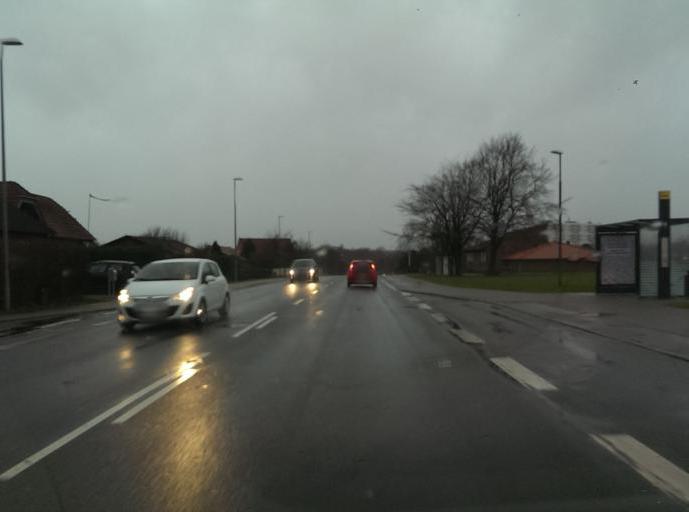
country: DK
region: South Denmark
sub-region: Esbjerg Kommune
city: Esbjerg
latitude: 55.4918
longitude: 8.4544
